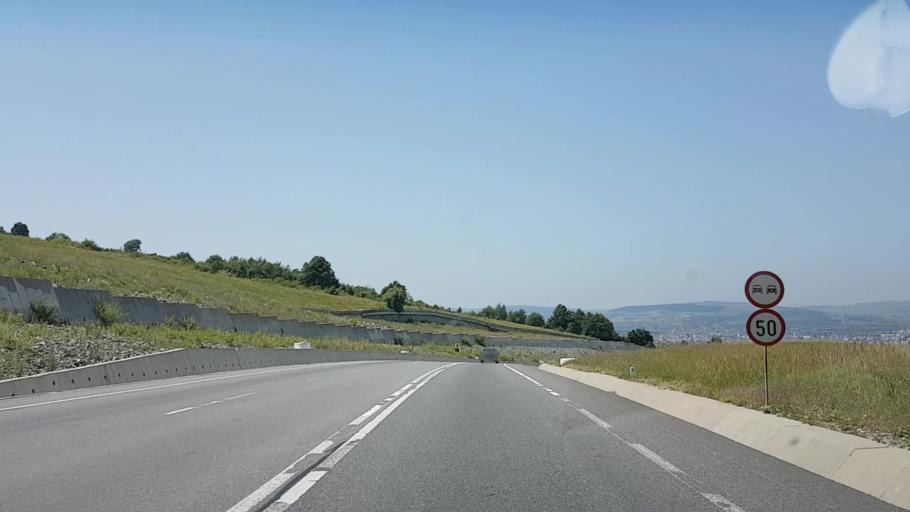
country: RO
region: Cluj
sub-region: Comuna Feleacu
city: Feleacu
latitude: 46.7217
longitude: 23.6479
